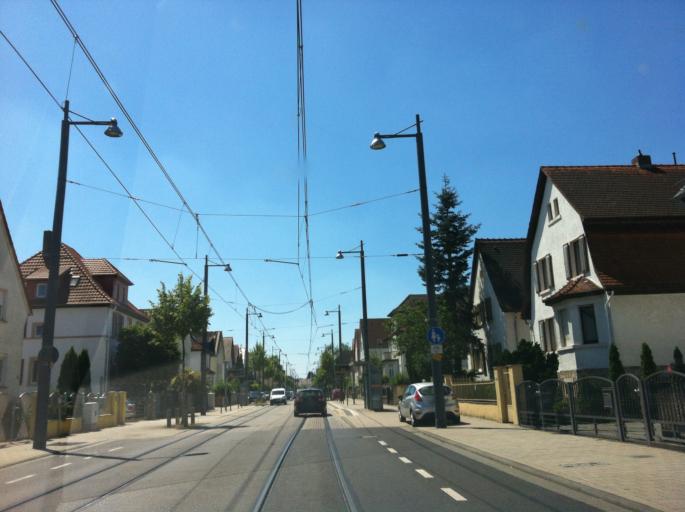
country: DE
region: Hesse
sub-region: Regierungsbezirk Darmstadt
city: Erzhausen
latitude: 49.9175
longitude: 8.6552
